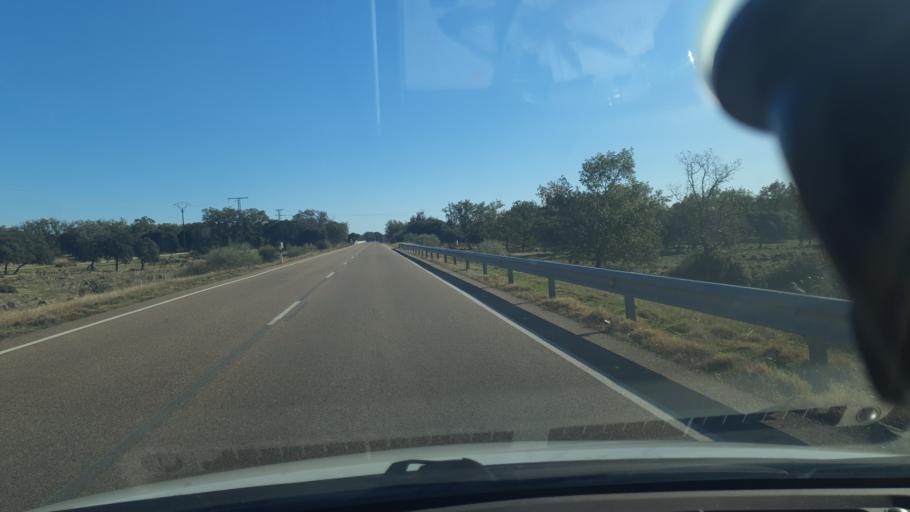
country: ES
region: Castille and Leon
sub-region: Provincia de Avila
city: Candeleda
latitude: 40.1399
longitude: -5.2561
